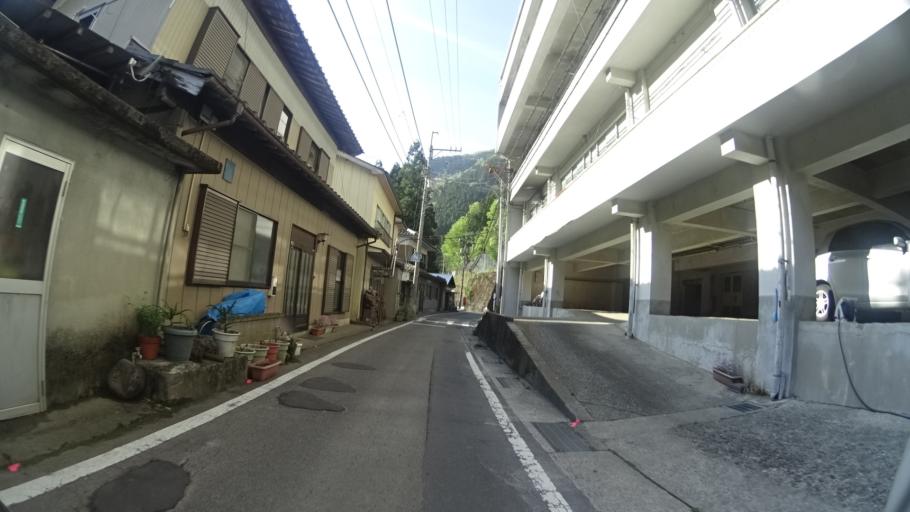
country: JP
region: Tokushima
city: Ikedacho
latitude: 33.8778
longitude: 133.9381
